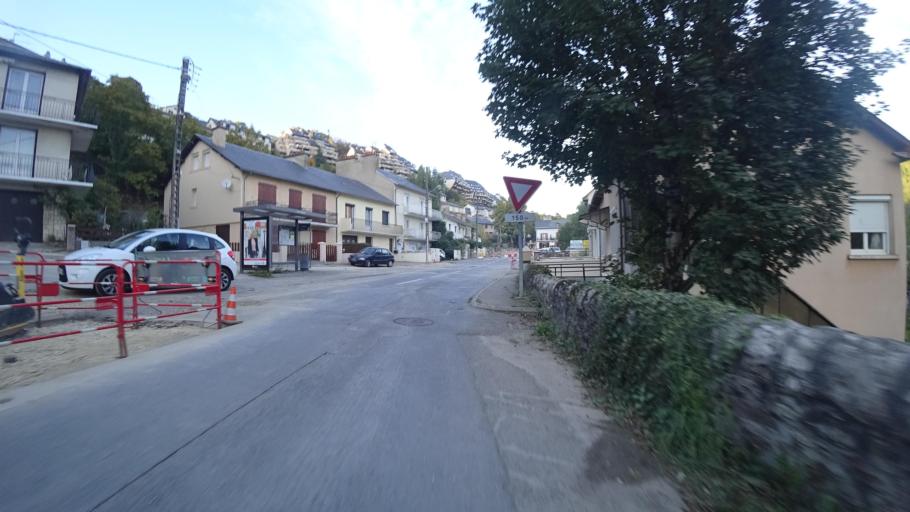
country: FR
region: Midi-Pyrenees
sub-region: Departement de l'Aveyron
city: Le Monastere
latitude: 44.3448
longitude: 2.5793
